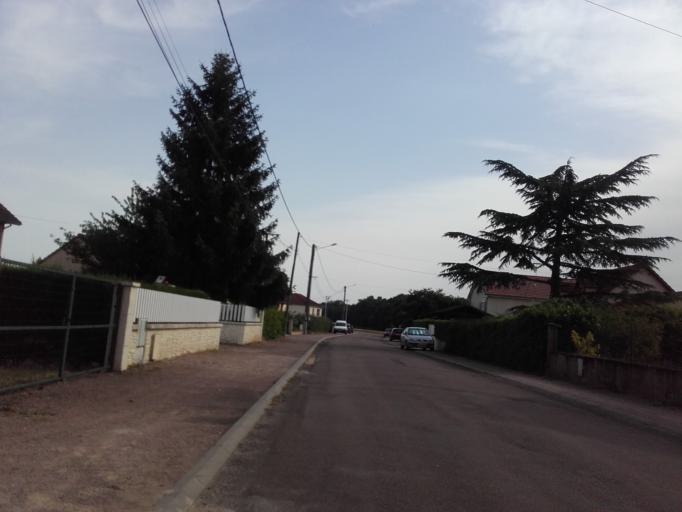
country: FR
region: Bourgogne
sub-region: Departement de Saone-et-Loire
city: Chagny
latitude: 46.8974
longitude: 4.7585
